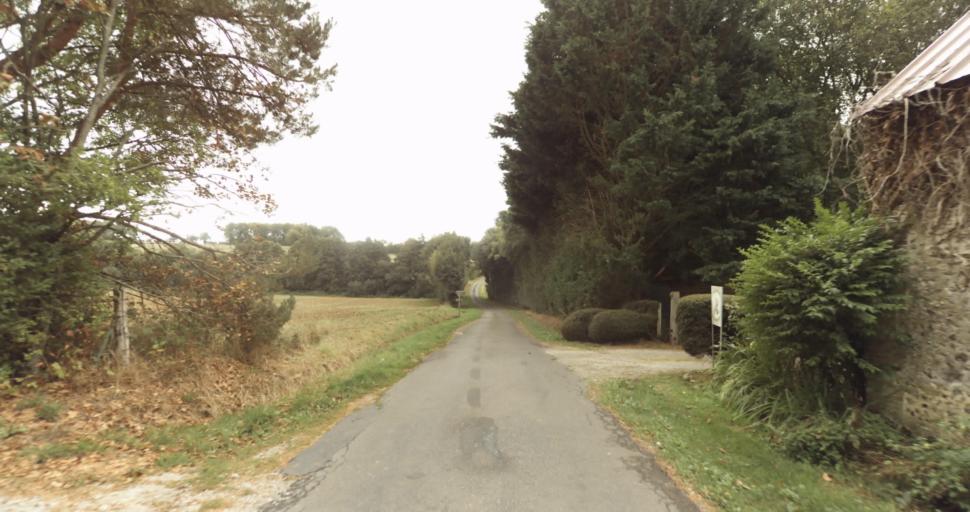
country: FR
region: Lower Normandy
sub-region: Departement de l'Orne
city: Sainte-Gauburge-Sainte-Colombe
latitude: 48.7223
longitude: 0.4794
